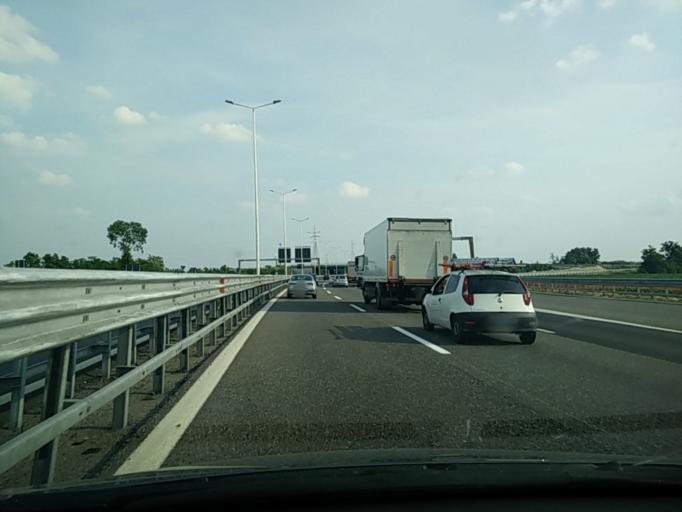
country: IT
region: Lombardy
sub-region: Citta metropolitana di Milano
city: Figino
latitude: 45.5014
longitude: 9.0665
